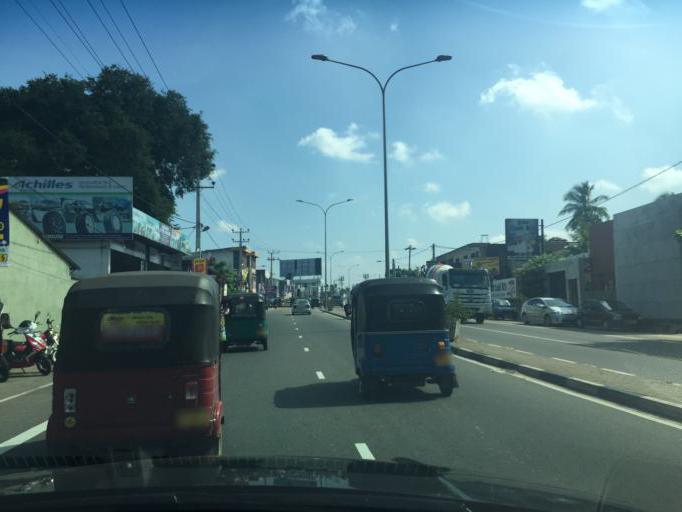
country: LK
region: Western
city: Maharagama
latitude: 6.8293
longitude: 79.9117
